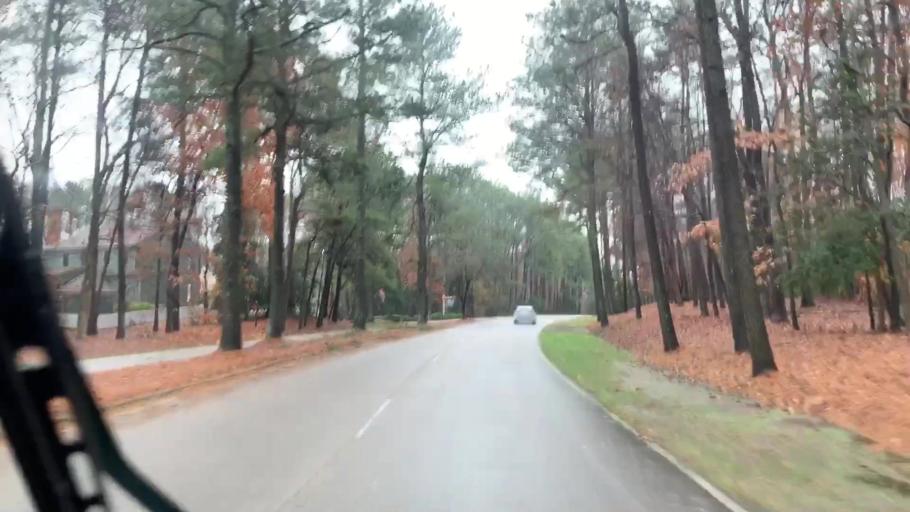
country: US
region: Virginia
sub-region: City of Williamsburg
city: Williamsburg
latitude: 37.2429
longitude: -76.6797
